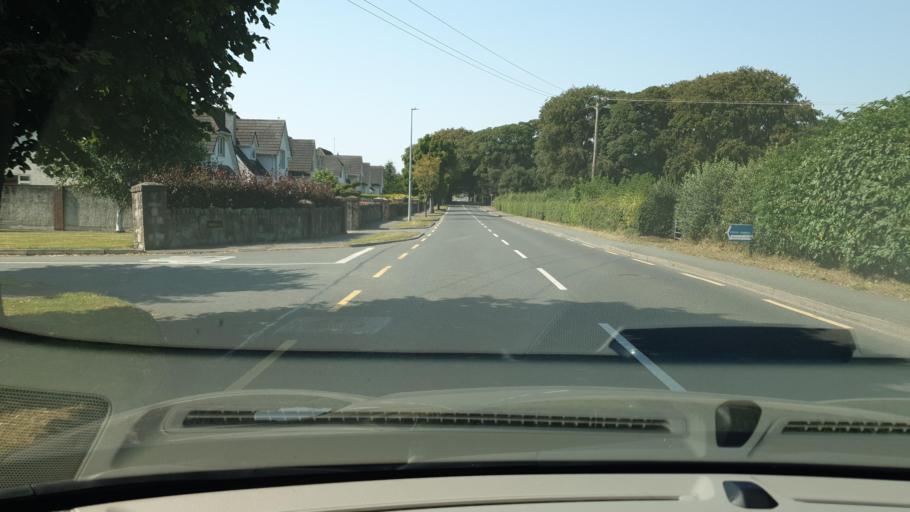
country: IE
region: Leinster
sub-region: An Mhi
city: Newtown Trim
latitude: 53.4842
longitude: -6.7357
